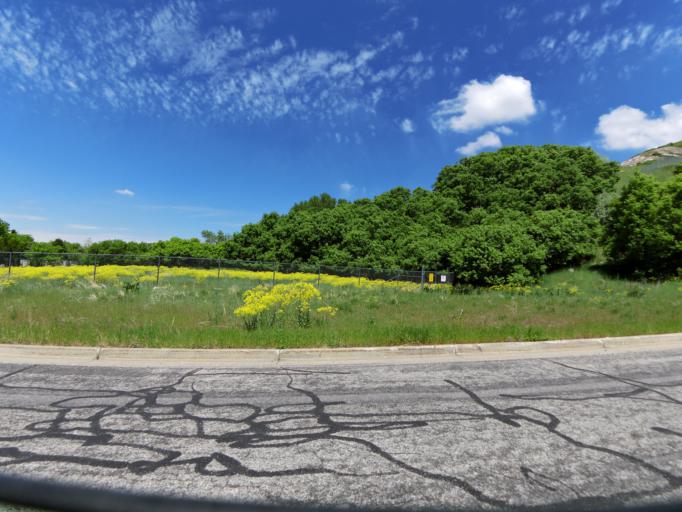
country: US
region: Utah
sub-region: Weber County
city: Uintah
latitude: 41.1634
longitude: -111.9234
